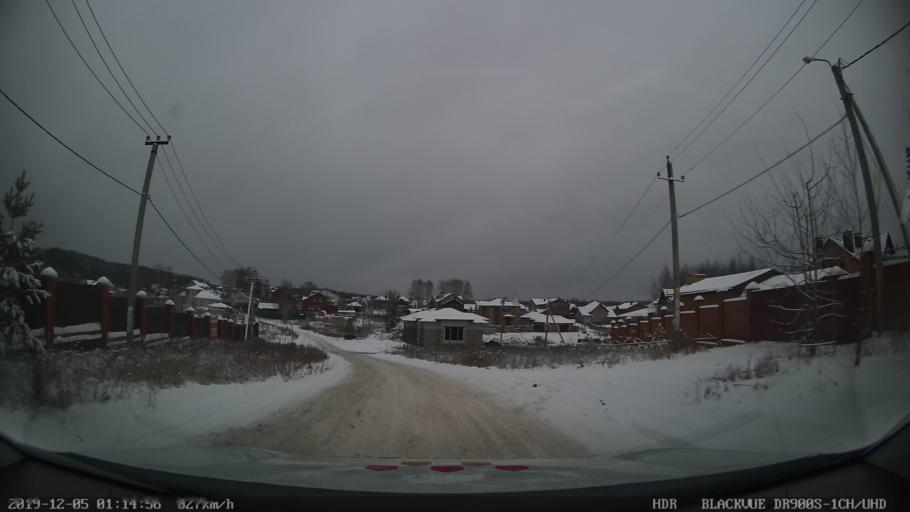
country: RU
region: Tatarstan
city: Stolbishchi
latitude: 55.6442
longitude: 49.1142
